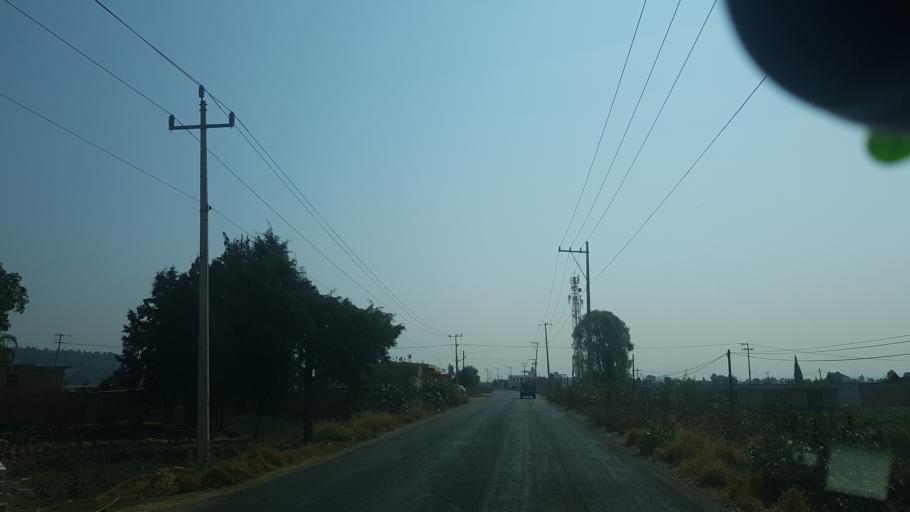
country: MX
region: Puebla
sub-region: San Jeronimo Tecuanipan
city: Los Reyes Tlanechicolpan
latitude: 19.0508
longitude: -98.3490
